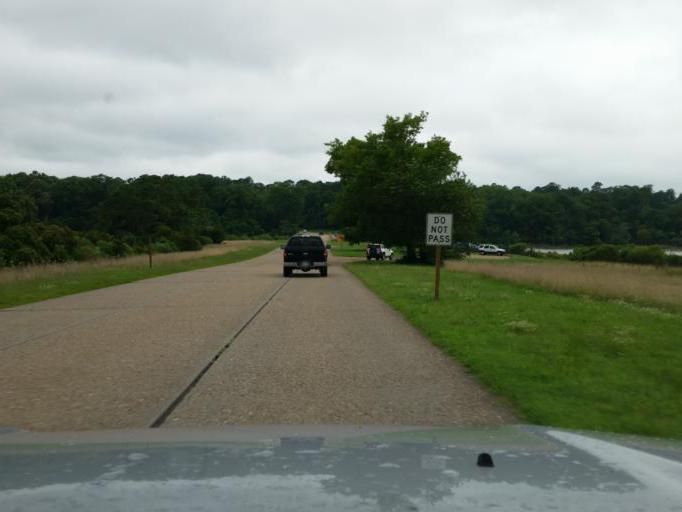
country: US
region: Virginia
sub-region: York County
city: Yorktown
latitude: 37.2733
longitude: -76.5830
